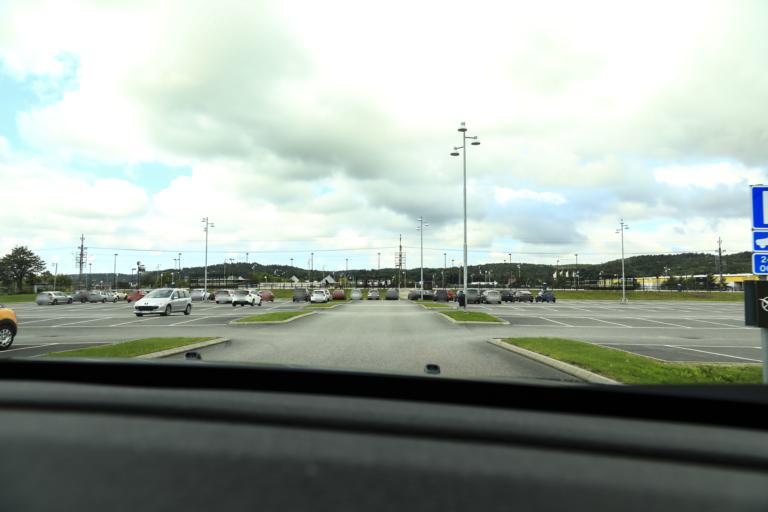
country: SE
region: Halland
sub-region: Kungsbacka Kommun
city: Kungsbacka
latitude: 57.5130
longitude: 12.0854
